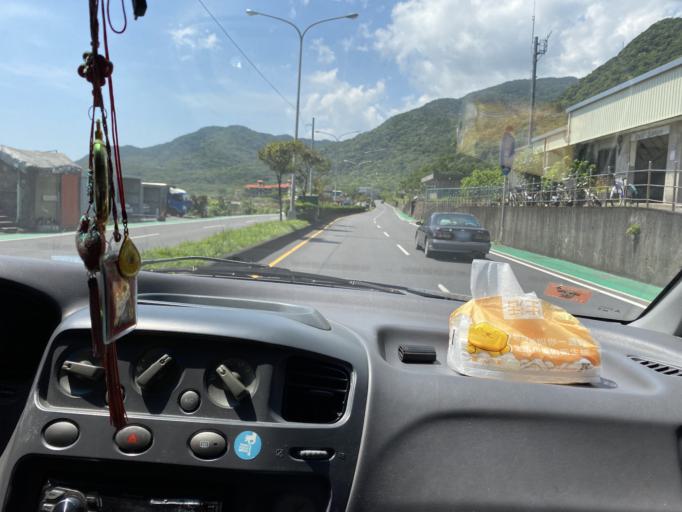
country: TW
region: Taiwan
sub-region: Yilan
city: Yilan
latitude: 24.9385
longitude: 121.8902
